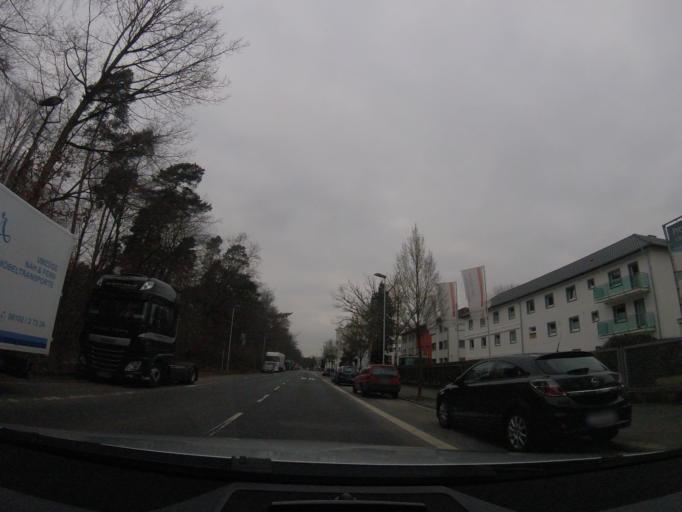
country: DE
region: Hesse
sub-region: Regierungsbezirk Darmstadt
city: Neu Isenburg
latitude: 50.0428
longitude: 8.6783
